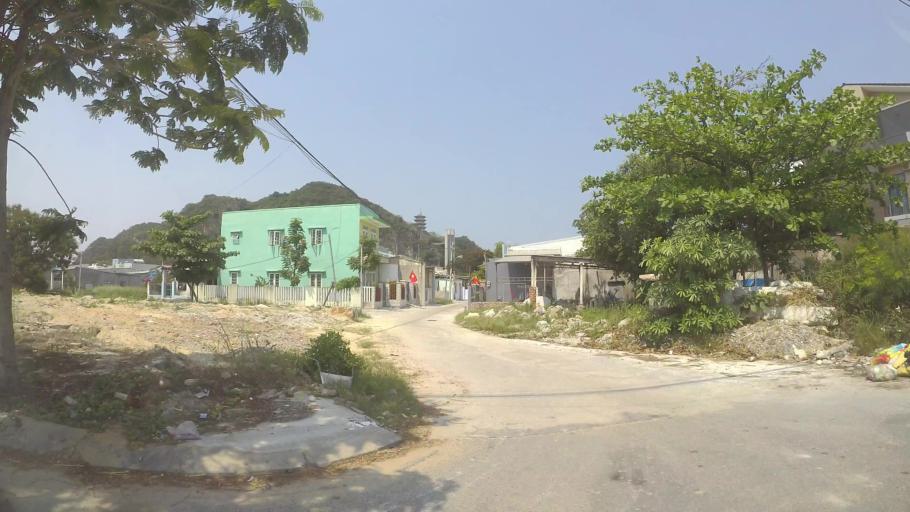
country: VN
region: Da Nang
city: Ngu Hanh Son
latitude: 16.0004
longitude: 108.2639
